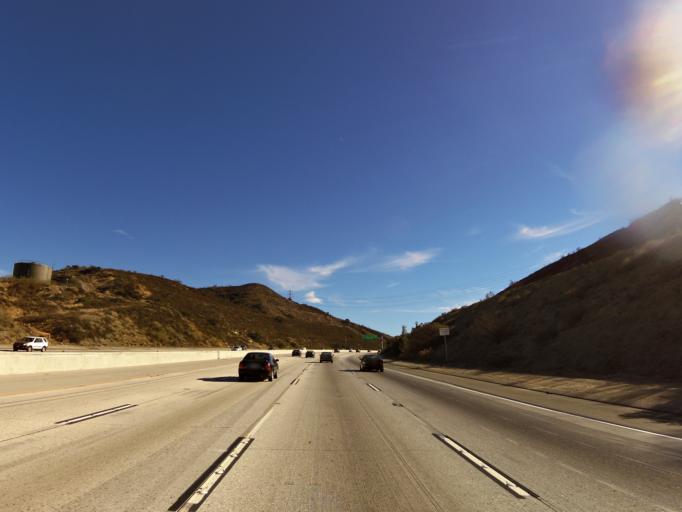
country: US
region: California
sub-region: Los Angeles County
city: Burbank
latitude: 34.2548
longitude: -118.3255
